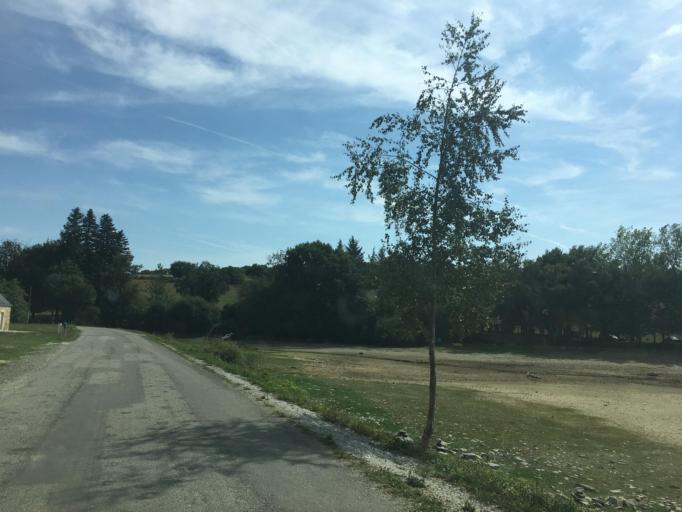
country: FR
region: Brittany
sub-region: Departement des Cotes-d'Armor
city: Mur-de-Bretagne
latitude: 48.2110
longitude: -3.0114
